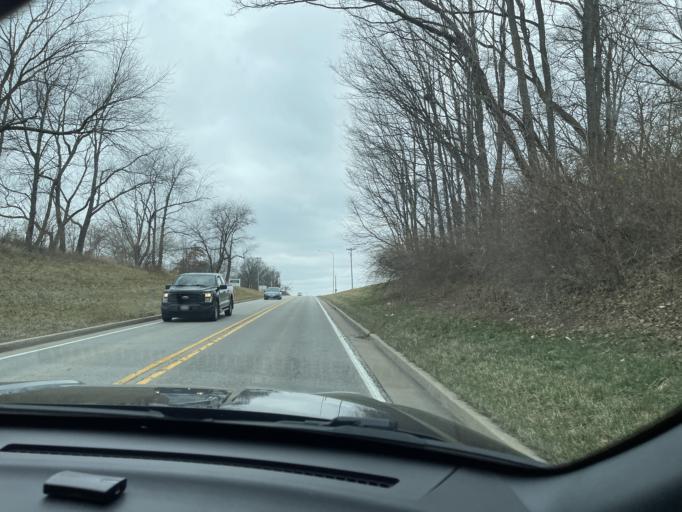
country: US
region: Illinois
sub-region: Sangamon County
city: Leland Grove
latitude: 39.8185
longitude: -89.7116
